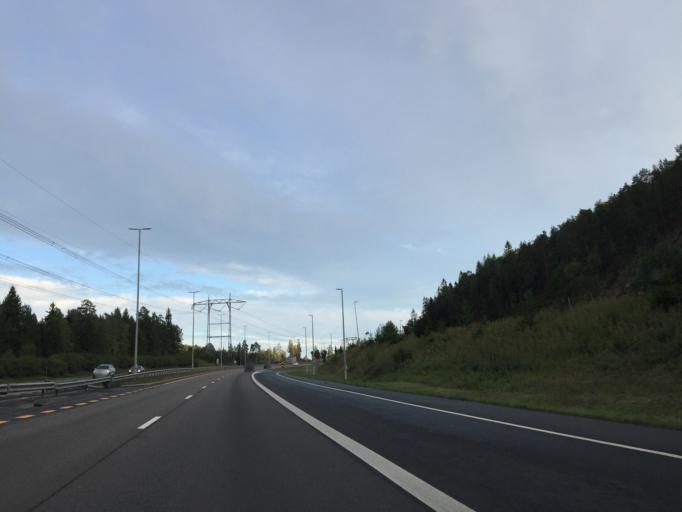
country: NO
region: Akershus
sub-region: Oppegard
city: Kolbotn
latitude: 59.8219
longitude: 10.8459
